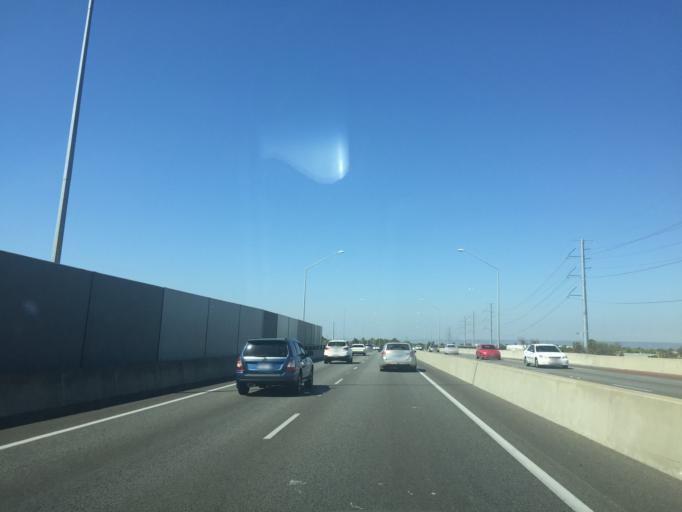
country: AU
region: Western Australia
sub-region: Canning
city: Willetton
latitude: -32.0701
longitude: 115.8891
